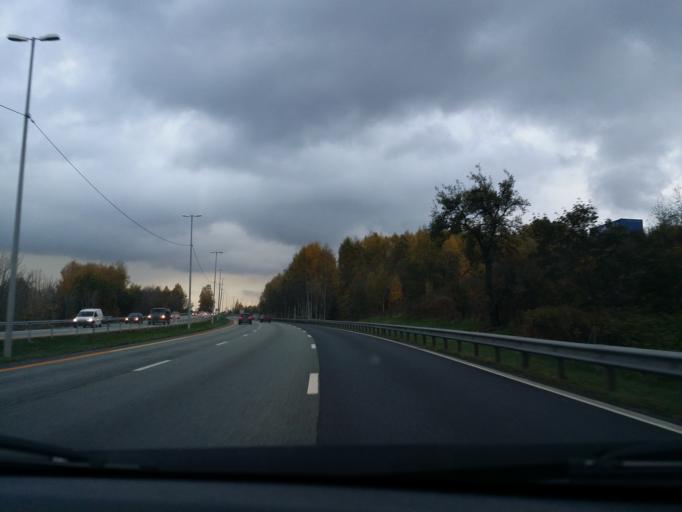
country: NO
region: Buskerud
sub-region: Lier
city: Tranby
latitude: 59.7796
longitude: 10.2767
